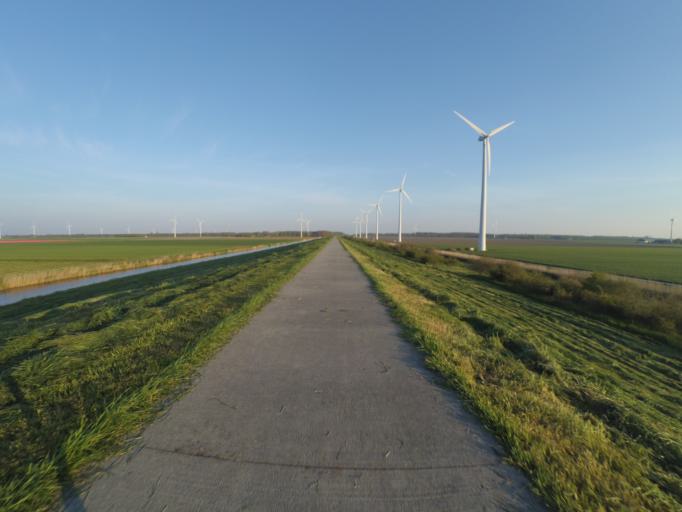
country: NL
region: Flevoland
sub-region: Gemeente Zeewolde
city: Zeewolde
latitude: 52.3911
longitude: 5.5222
